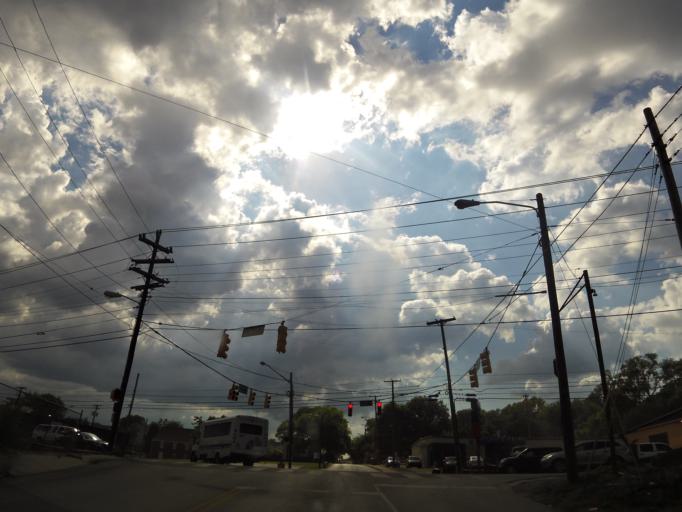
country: US
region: Tennessee
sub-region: Davidson County
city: Nashville
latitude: 36.2050
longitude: -86.7373
